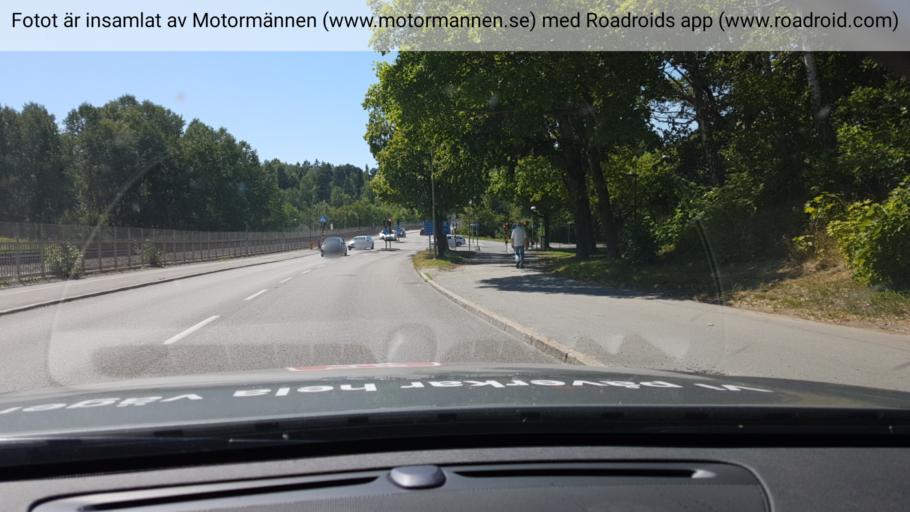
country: SE
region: Stockholm
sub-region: Stockholms Kommun
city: Arsta
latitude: 59.2609
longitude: 18.0395
